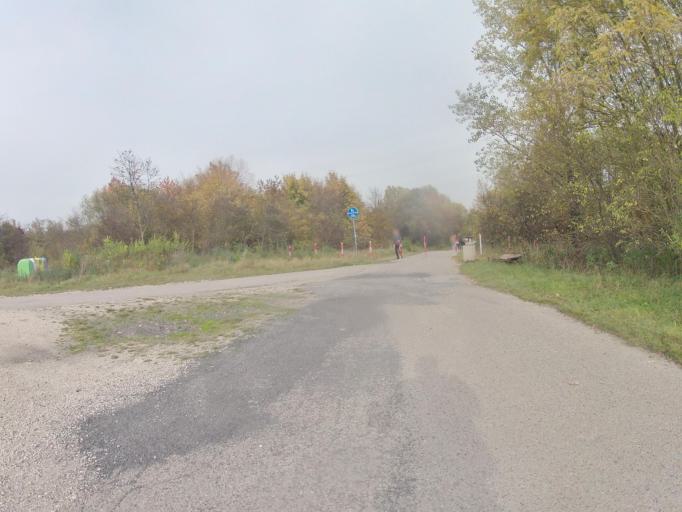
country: PL
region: Lesser Poland Voivodeship
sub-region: Krakow
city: Krakow
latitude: 50.0357
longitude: 19.9136
